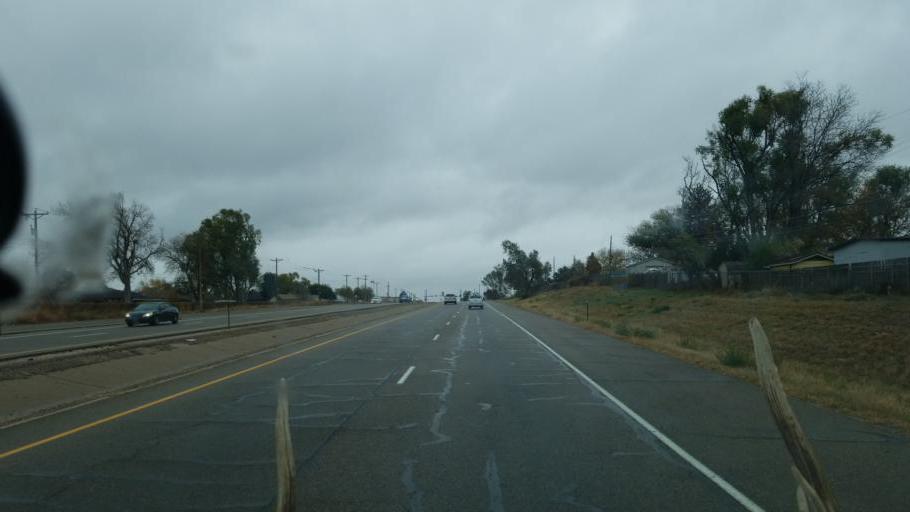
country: US
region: Colorado
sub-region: Pueblo County
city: Pueblo
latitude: 38.2860
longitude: -104.5924
